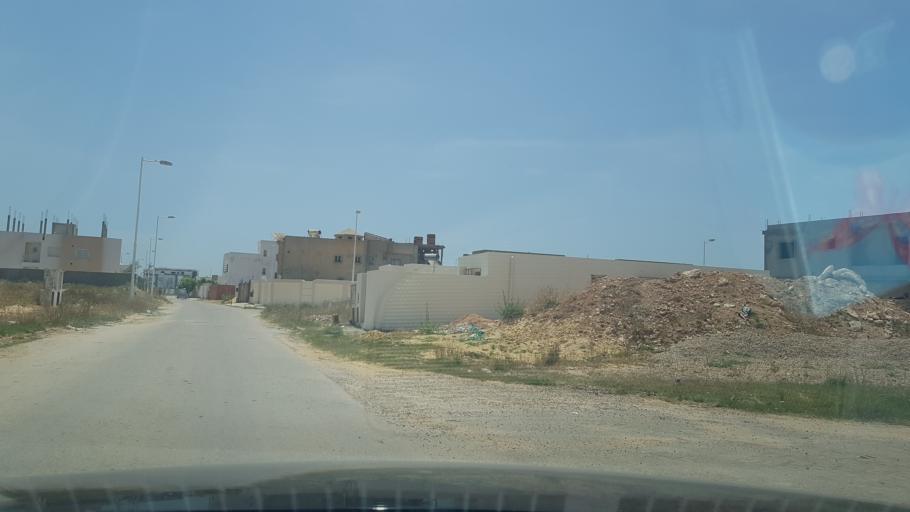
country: TN
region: Safaqis
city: Al Qarmadah
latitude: 34.8409
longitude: 10.7588
